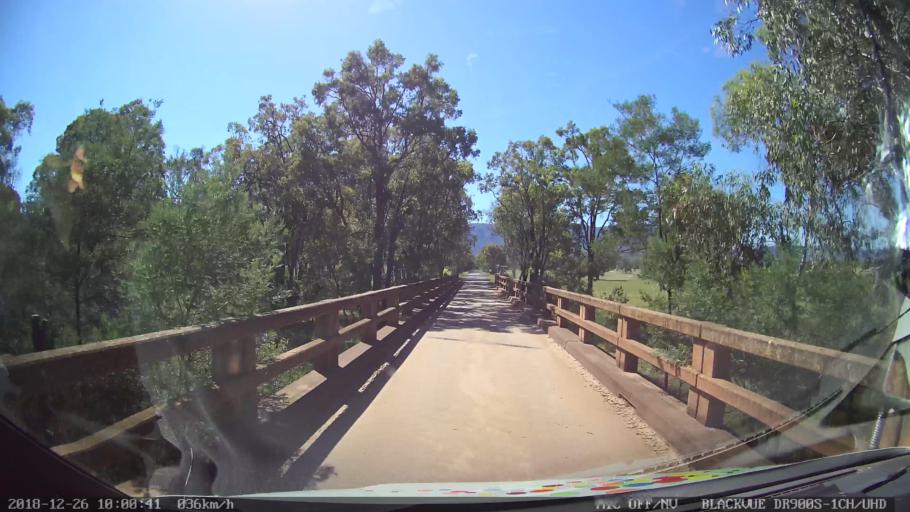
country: AU
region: New South Wales
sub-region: Mid-Western Regional
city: Kandos
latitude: -33.0444
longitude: 150.2174
